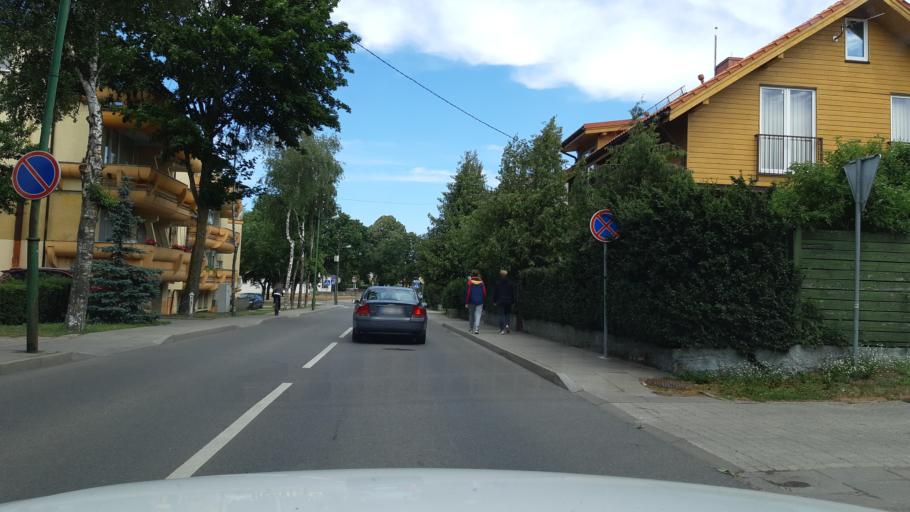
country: LT
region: Klaipedos apskritis
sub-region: Klaipeda
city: Palanga
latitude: 55.9135
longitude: 21.0685
